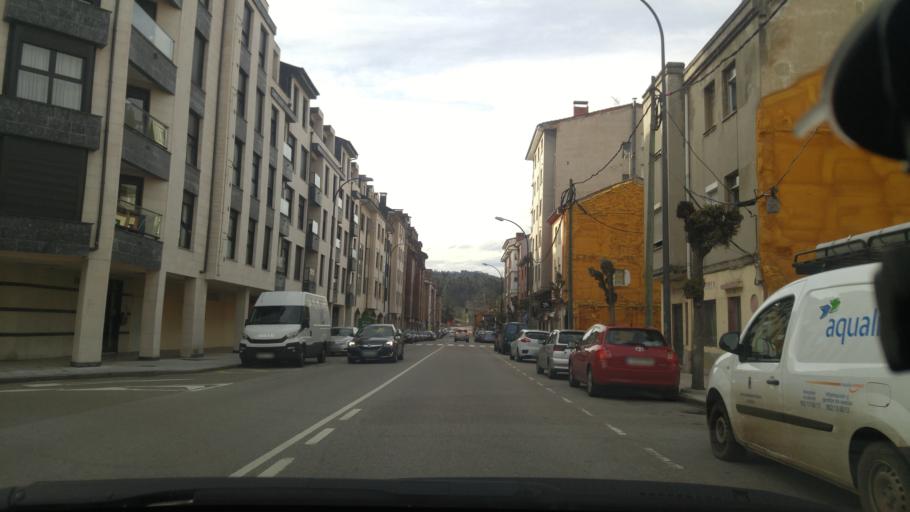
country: ES
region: Asturias
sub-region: Province of Asturias
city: Llanera
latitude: 43.4413
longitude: -5.8532
